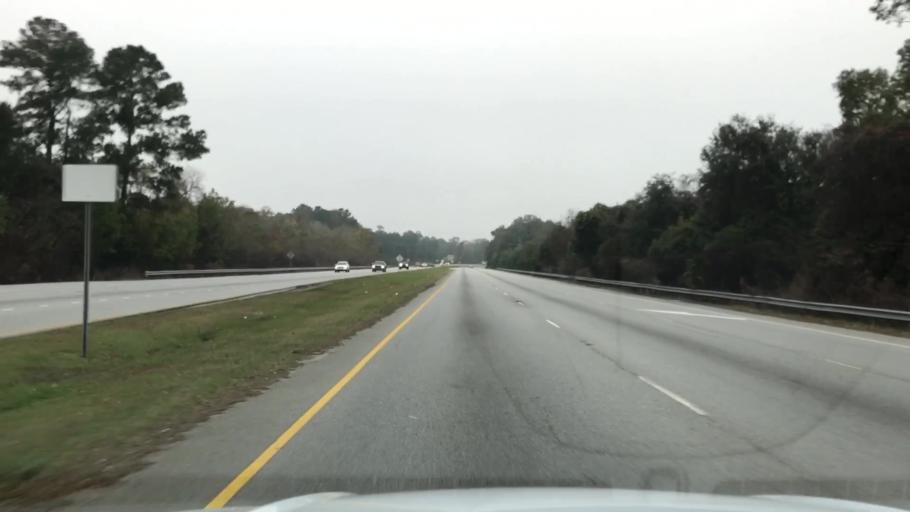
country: US
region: South Carolina
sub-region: Charleston County
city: Shell Point
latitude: 32.8121
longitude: -80.0477
